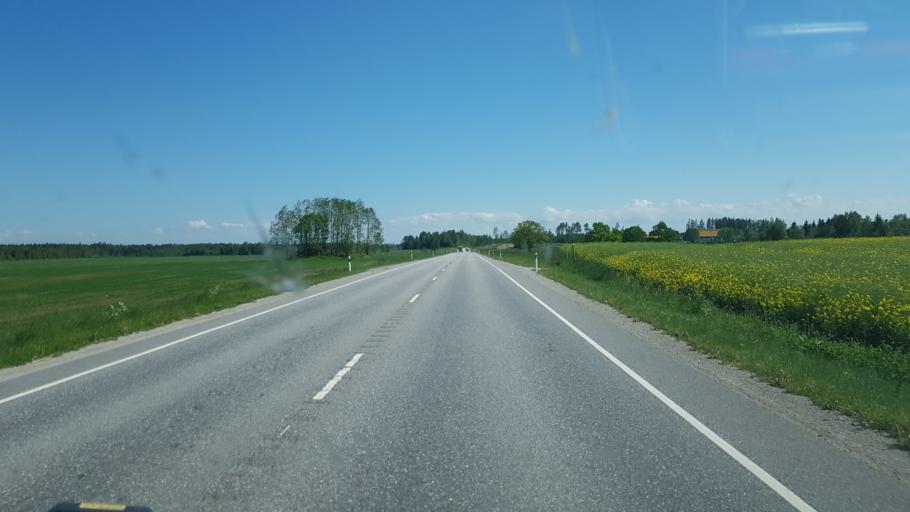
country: EE
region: Laeaene-Virumaa
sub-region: Someru vald
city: Someru
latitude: 59.3504
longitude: 26.4018
